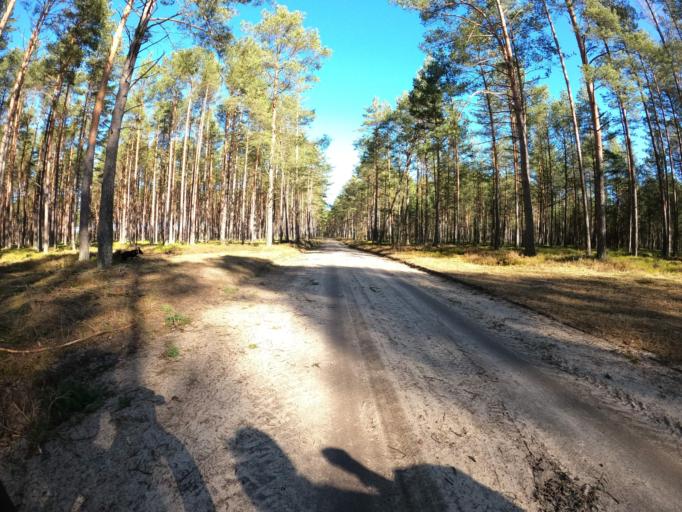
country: PL
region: Greater Poland Voivodeship
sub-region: Powiat zlotowski
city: Sypniewo
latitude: 53.5099
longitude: 16.6454
